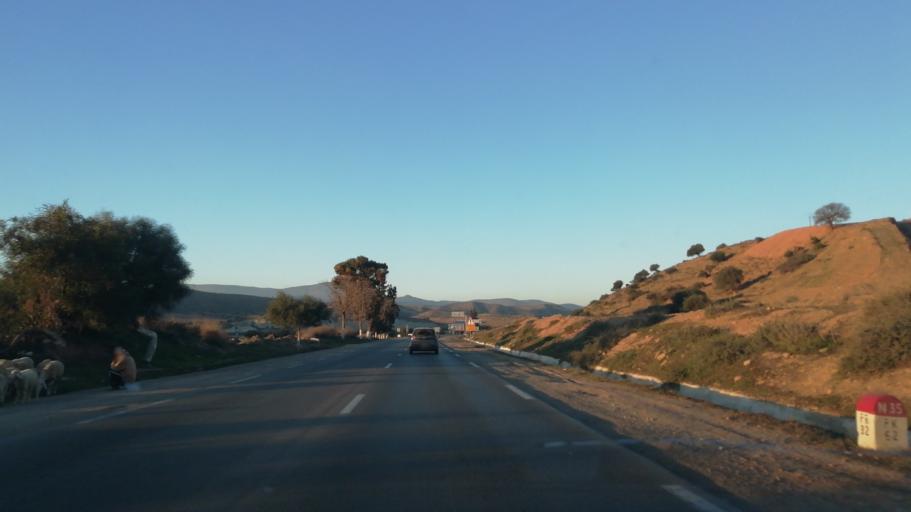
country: DZ
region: Tlemcen
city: Nedroma
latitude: 34.9033
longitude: -1.6402
